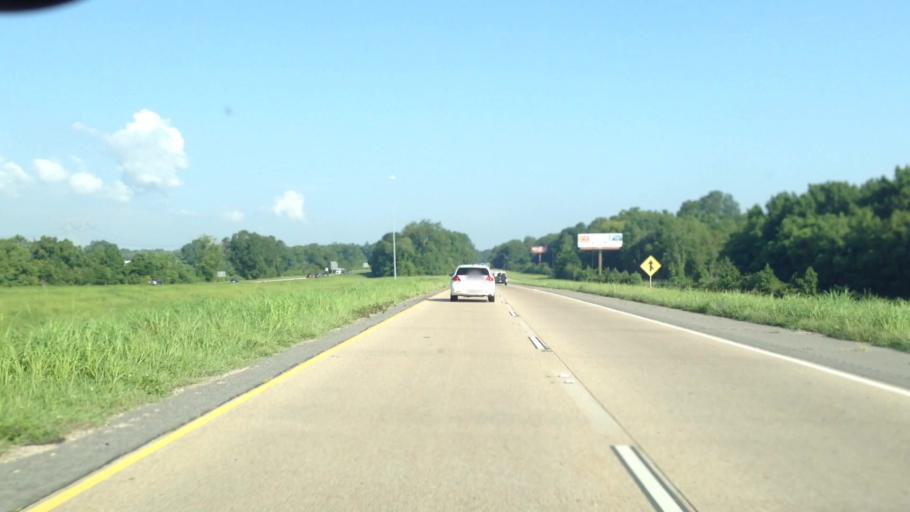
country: US
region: Louisiana
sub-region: Ascension Parish
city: Gonzales
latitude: 30.1931
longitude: -90.9210
